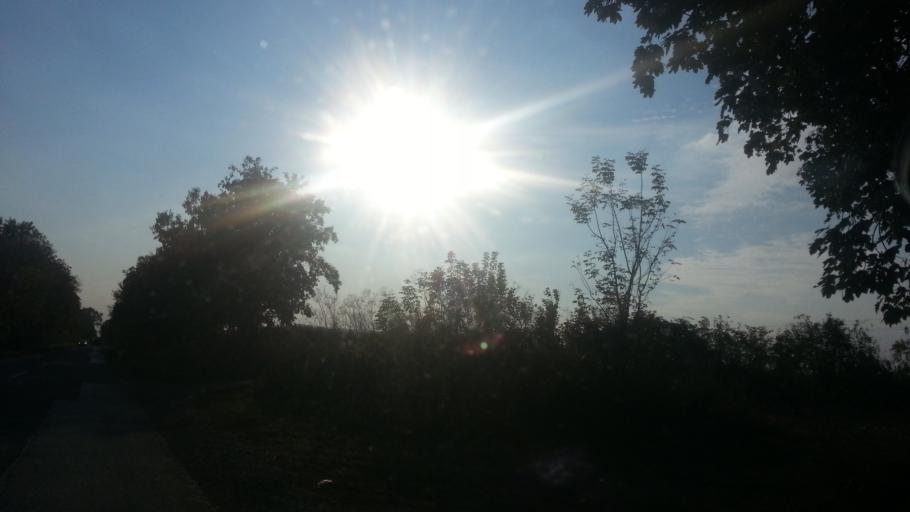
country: RS
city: Novi Slankamen
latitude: 45.1065
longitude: 20.2136
